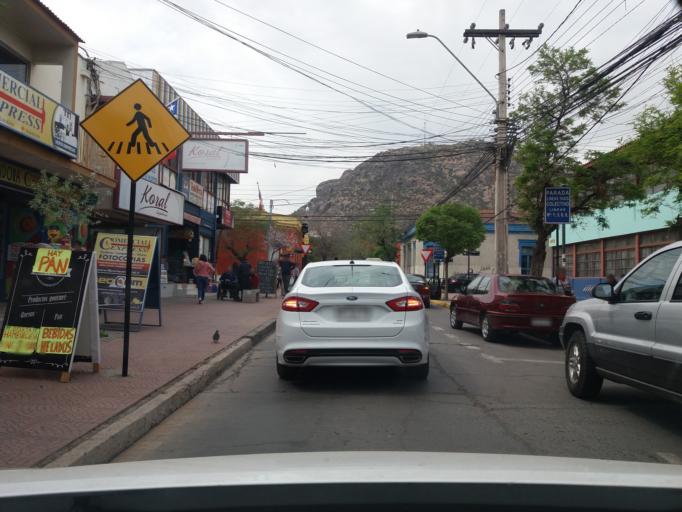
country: CL
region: Valparaiso
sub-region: Provincia de Los Andes
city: Los Andes
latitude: -32.8347
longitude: -70.5969
